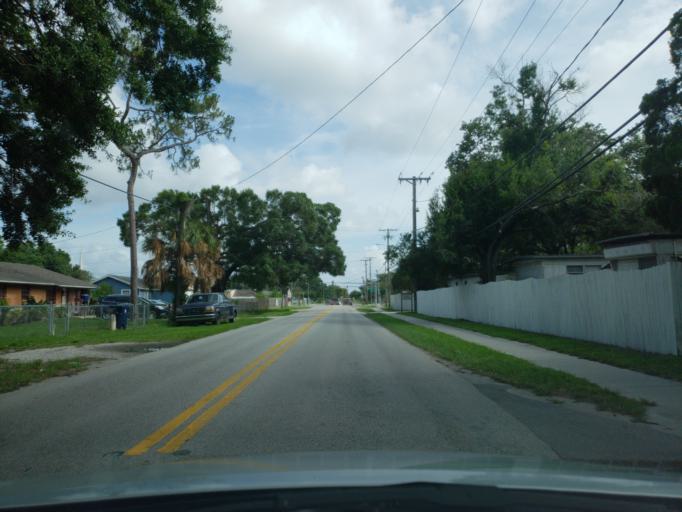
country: US
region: Florida
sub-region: Hillsborough County
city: Egypt Lake-Leto
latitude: 27.9975
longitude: -82.4762
